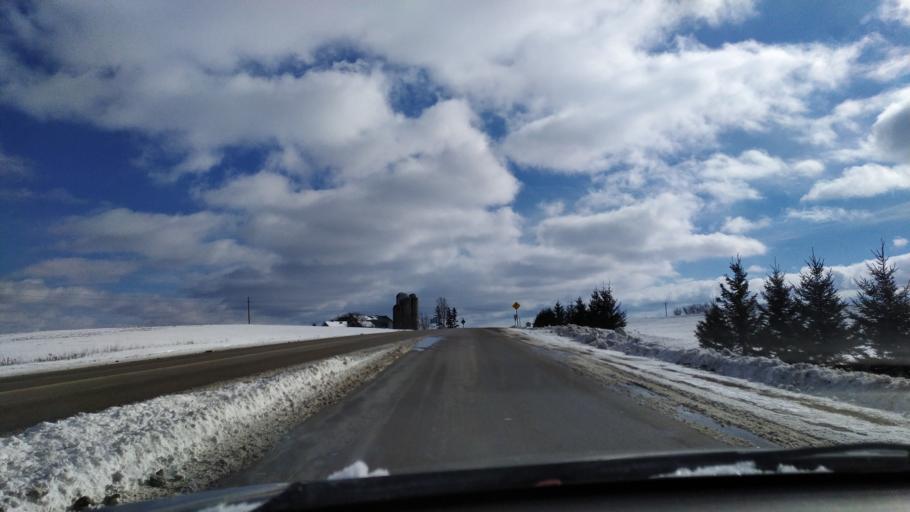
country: CA
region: Ontario
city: Waterloo
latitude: 43.5916
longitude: -80.6099
